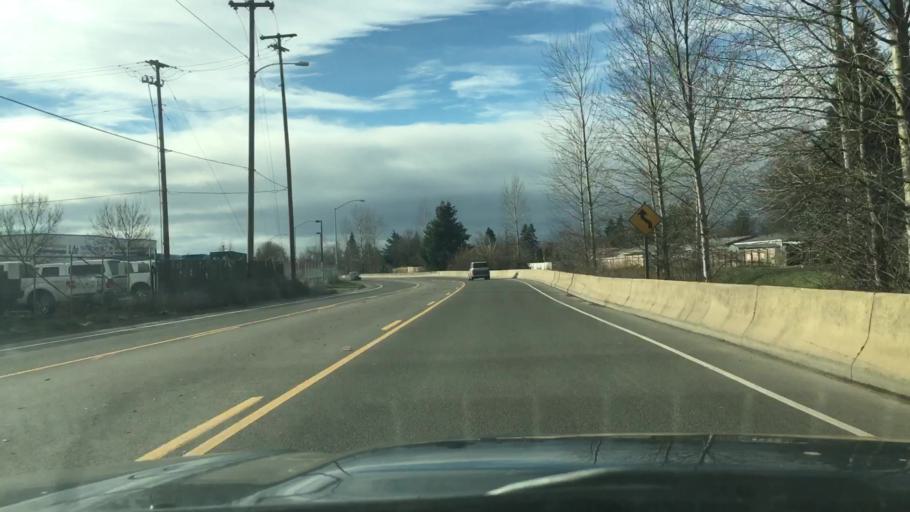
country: US
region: Oregon
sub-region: Lane County
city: Eugene
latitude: 44.0638
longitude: -123.1462
